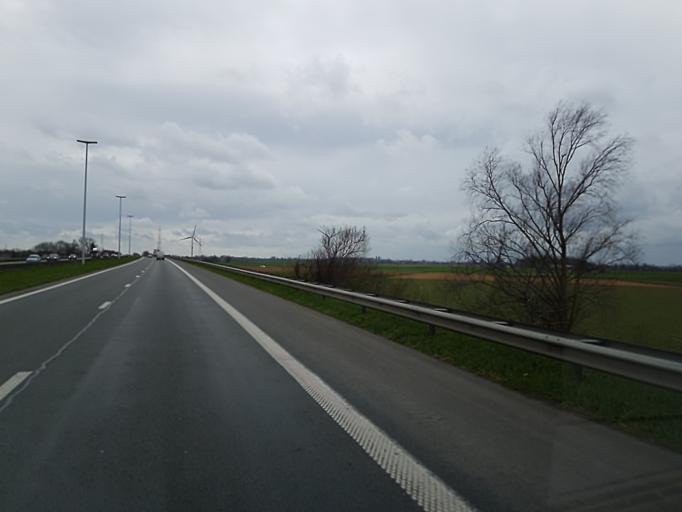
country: BE
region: Wallonia
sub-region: Province du Hainaut
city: Estaimpuis
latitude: 50.6925
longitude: 3.2930
